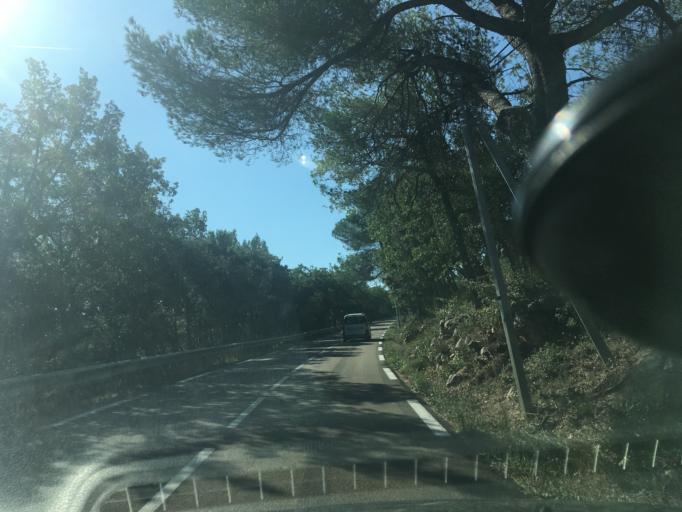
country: FR
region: Provence-Alpes-Cote d'Azur
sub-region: Departement du Var
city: Regusse
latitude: 43.6107
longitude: 6.0689
